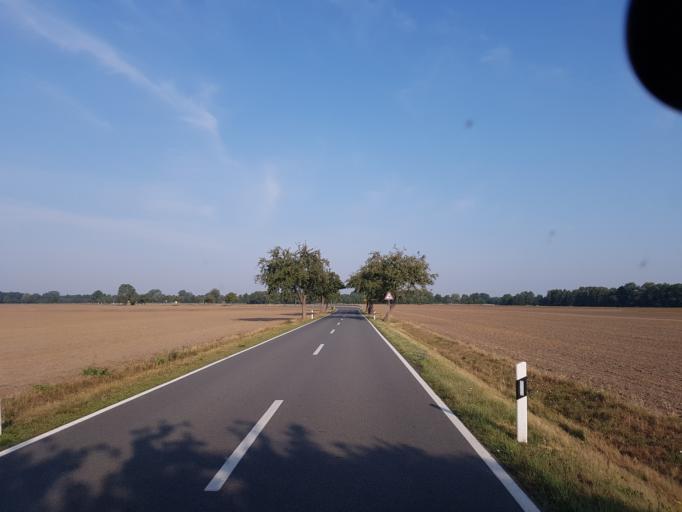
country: DE
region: Brandenburg
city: Finsterwalde
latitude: 51.6684
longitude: 13.7271
